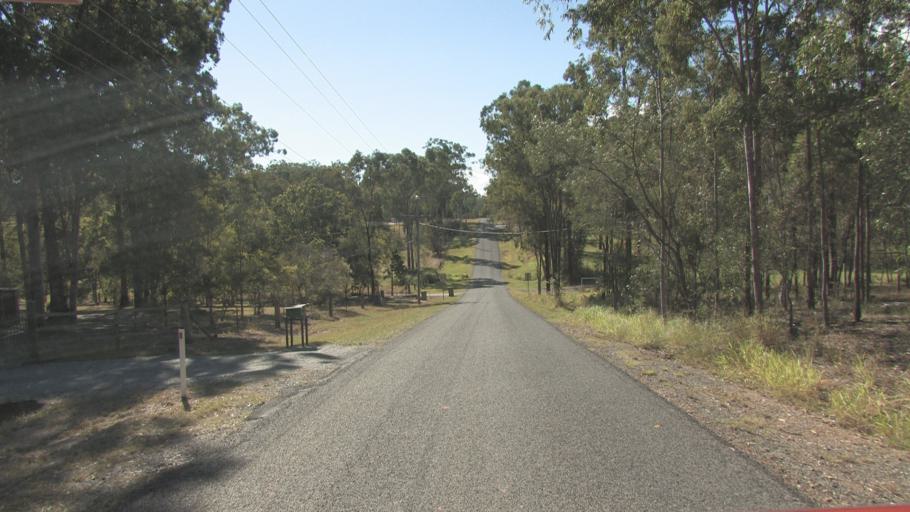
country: AU
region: Queensland
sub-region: Logan
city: Chambers Flat
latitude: -27.8117
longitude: 153.0782
